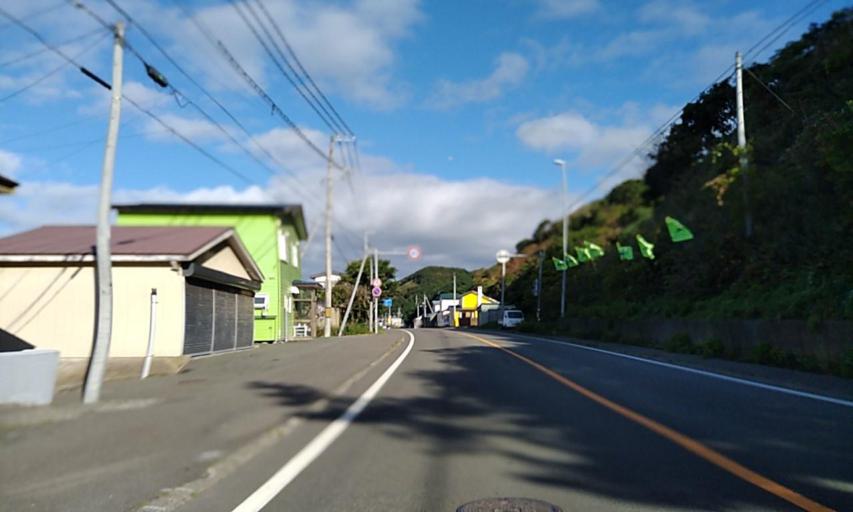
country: JP
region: Hokkaido
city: Shizunai-furukawacho
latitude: 42.2024
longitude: 142.6587
